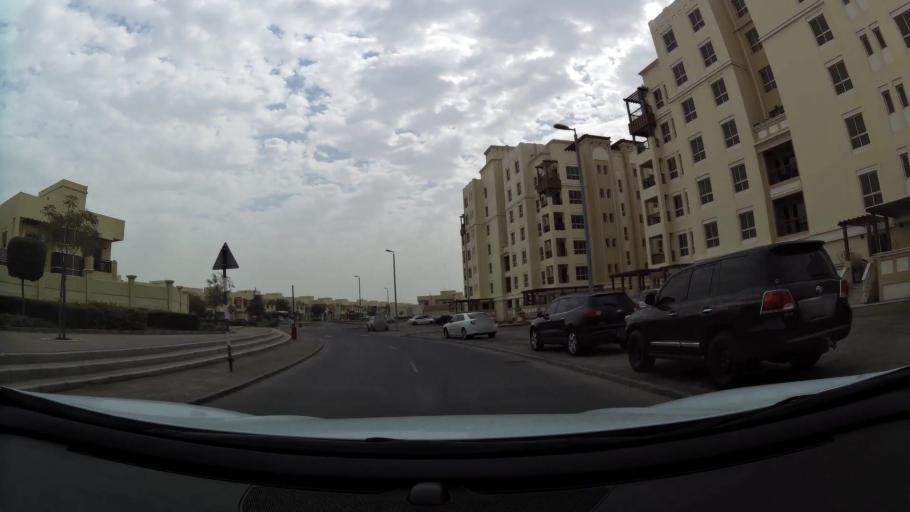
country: AE
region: Abu Dhabi
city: Abu Dhabi
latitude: 24.3140
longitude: 54.6226
